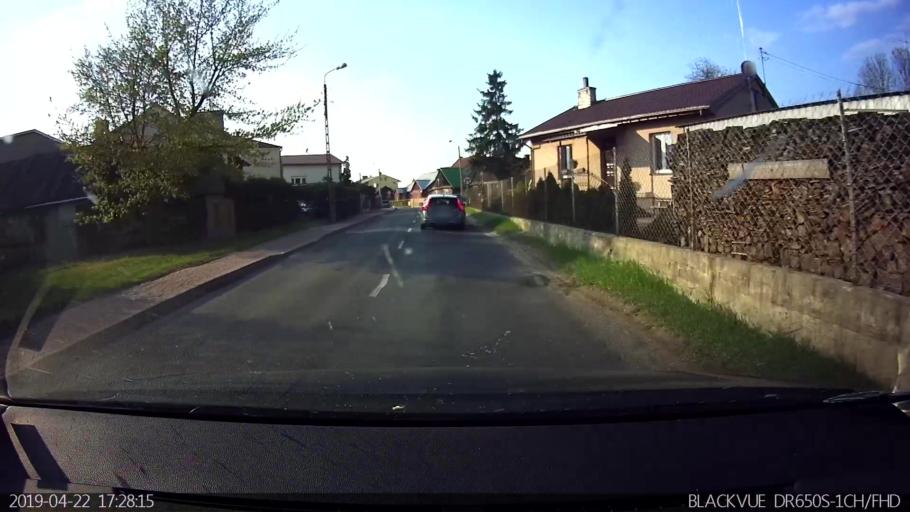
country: PL
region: Masovian Voivodeship
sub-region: Powiat sokolowski
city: Sokolow Podlaski
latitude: 52.4018
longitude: 22.2604
